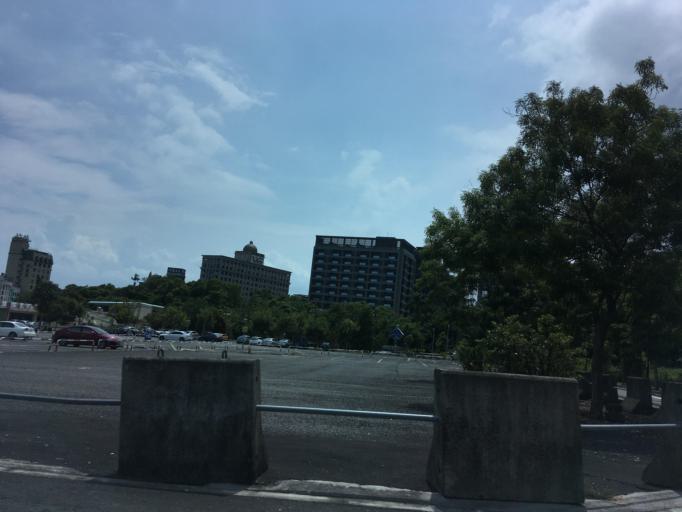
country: TW
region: Taiwan
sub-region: Yilan
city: Yilan
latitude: 24.8327
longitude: 121.7780
